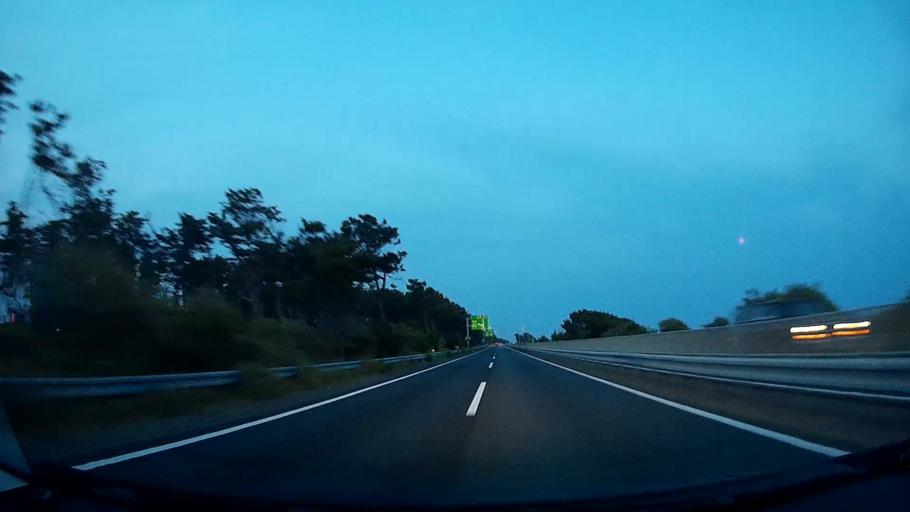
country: JP
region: Shizuoka
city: Kosai-shi
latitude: 34.6776
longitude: 137.6234
